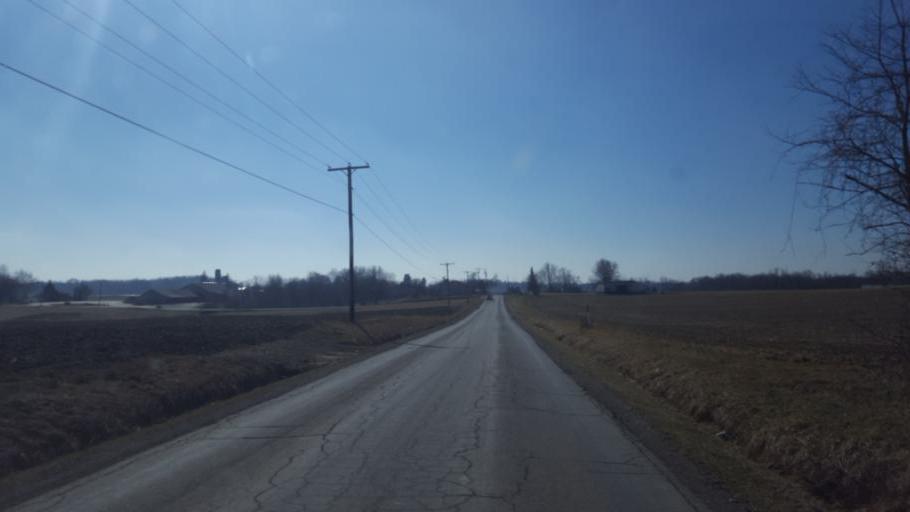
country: US
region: Ohio
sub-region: Huron County
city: Plymouth
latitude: 40.9625
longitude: -82.5847
